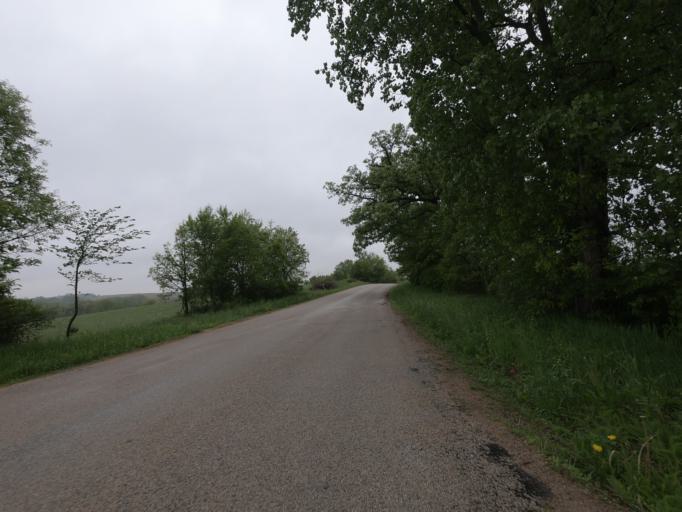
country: US
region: Wisconsin
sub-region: Grant County
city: Hazel Green
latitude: 42.4853
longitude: -90.4905
